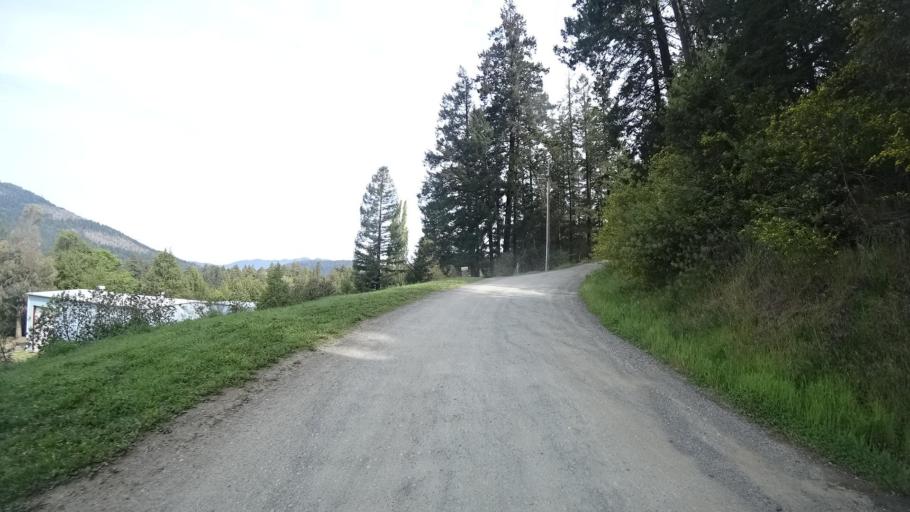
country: US
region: California
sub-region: Humboldt County
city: Redway
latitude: 40.2361
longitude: -123.8186
